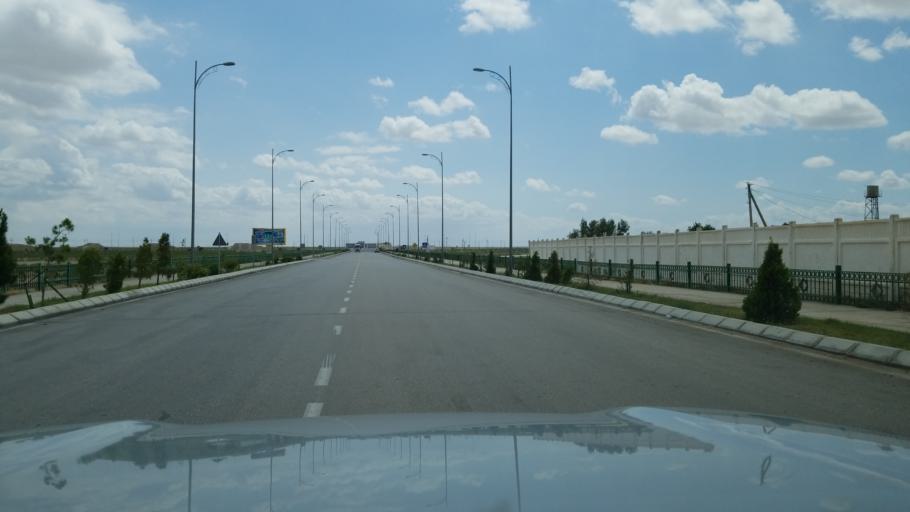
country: TM
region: Balkan
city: Balkanabat
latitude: 39.4901
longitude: 54.3771
